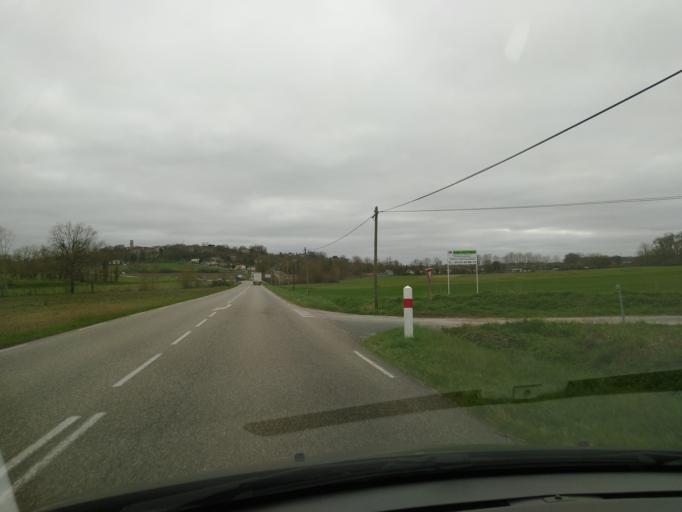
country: FR
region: Aquitaine
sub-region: Departement du Lot-et-Garonne
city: Castillonnes
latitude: 44.6635
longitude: 0.5845
